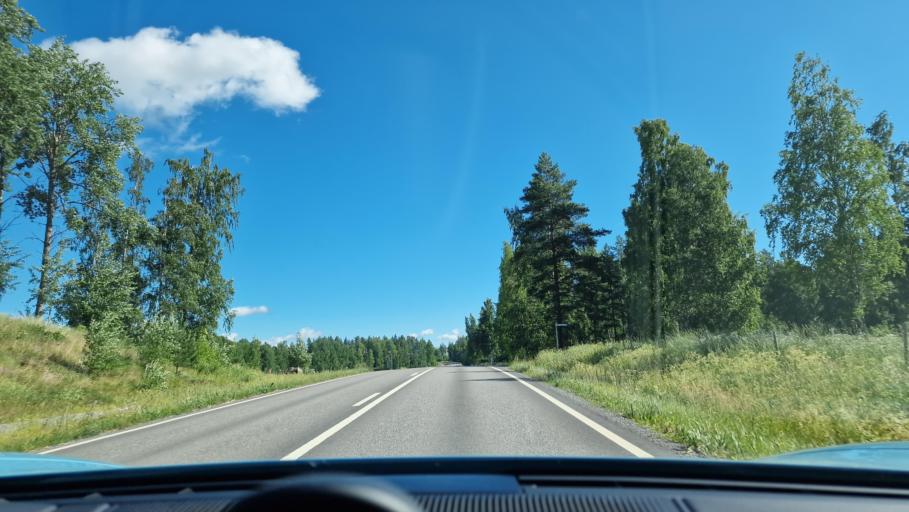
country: FI
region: Pirkanmaa
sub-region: Tampere
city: Kangasala
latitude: 61.4793
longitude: 24.1457
